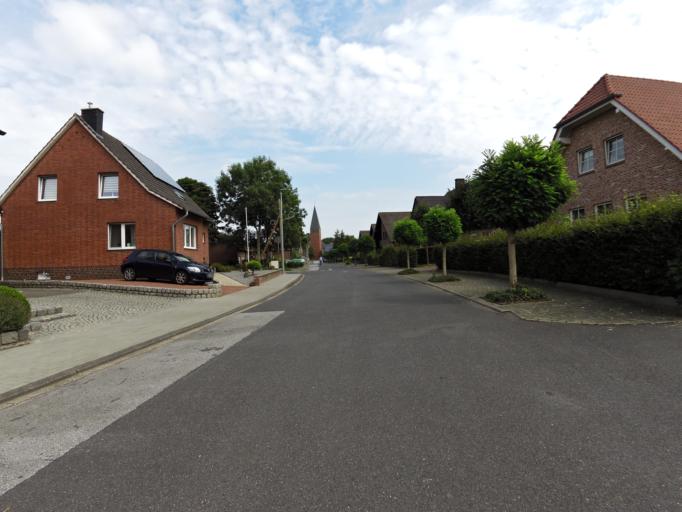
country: DE
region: North Rhine-Westphalia
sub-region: Regierungsbezirk Koln
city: Gangelt
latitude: 50.9851
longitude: 6.0337
